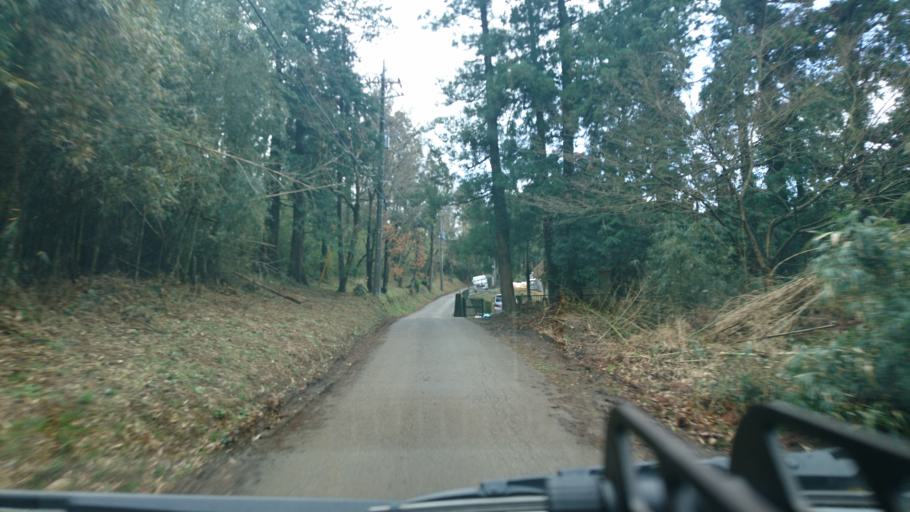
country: JP
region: Chiba
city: Kimitsu
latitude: 35.2949
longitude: 139.9661
